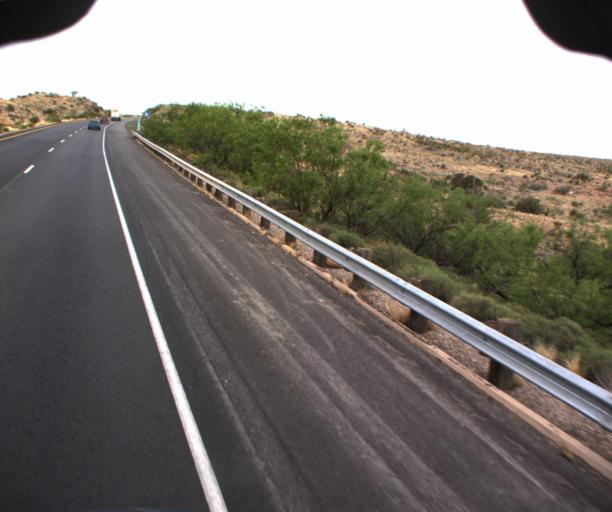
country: US
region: Arizona
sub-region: Pima County
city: Vail
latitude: 31.9970
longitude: -110.6527
